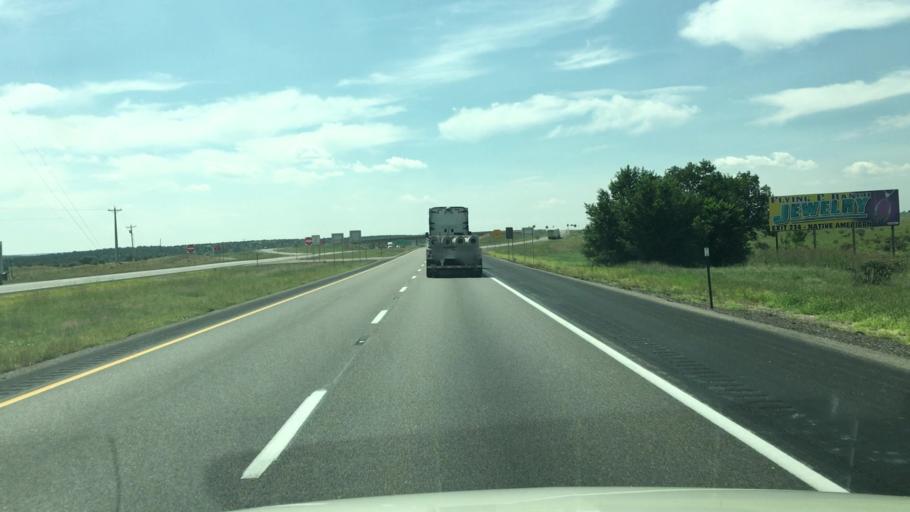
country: US
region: New Mexico
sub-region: San Miguel County
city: Las Vegas
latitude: 34.9913
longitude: -105.2877
